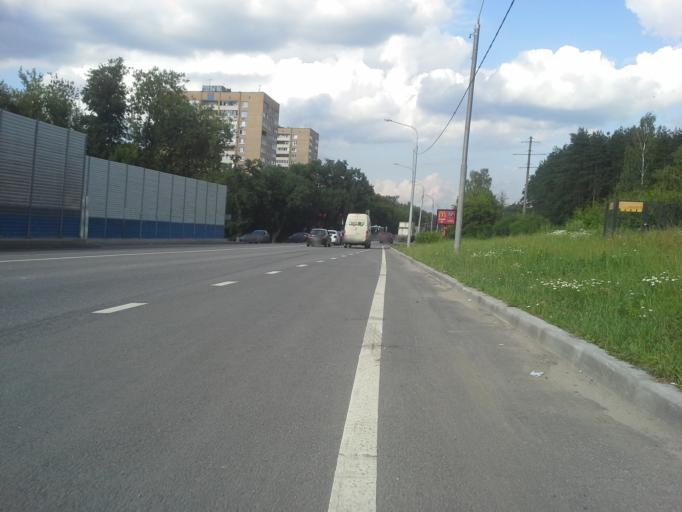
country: RU
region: Moskovskaya
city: Dubrovitsy
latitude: 55.4182
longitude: 37.5045
